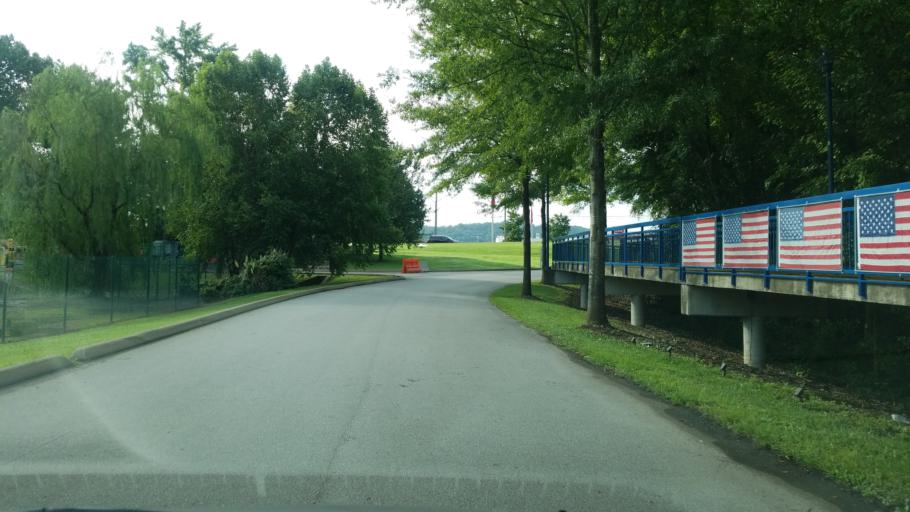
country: US
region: Tennessee
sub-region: Hamilton County
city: East Chattanooga
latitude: 35.0948
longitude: -85.2541
